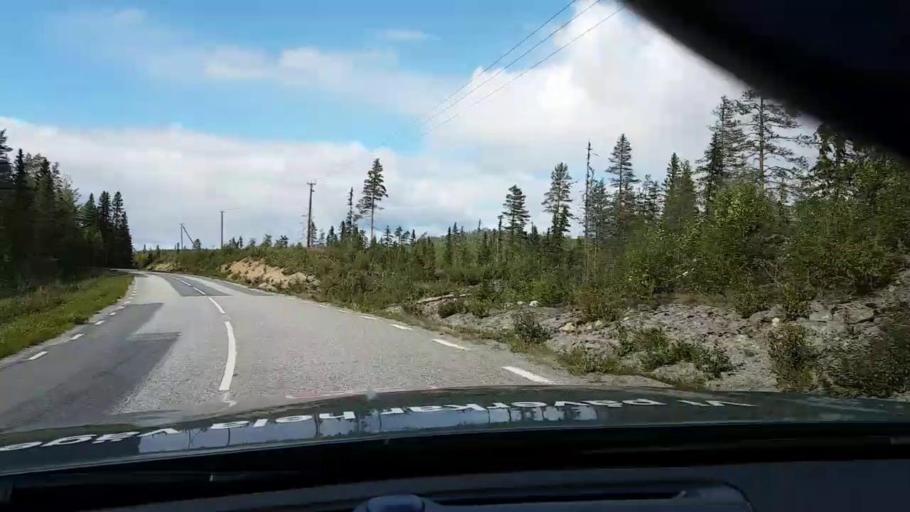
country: SE
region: Vaesterbotten
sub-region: Asele Kommun
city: Asele
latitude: 63.8255
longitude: 17.4759
